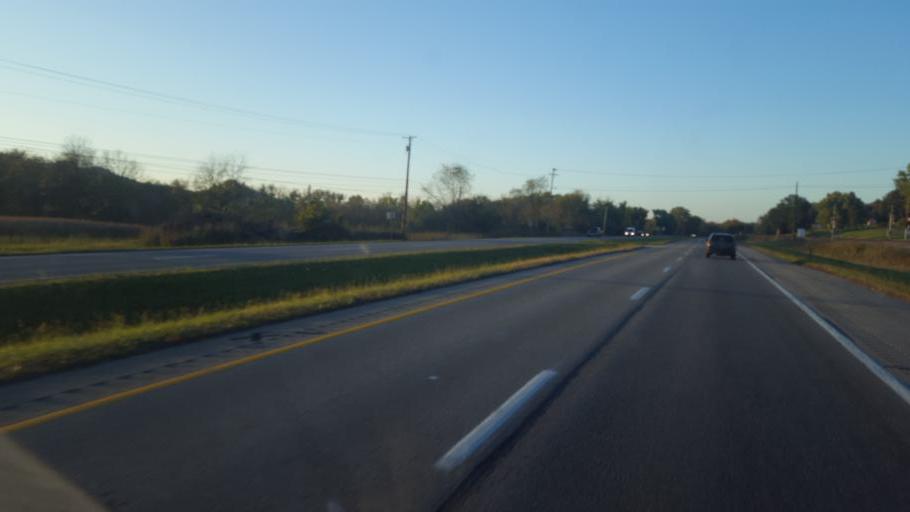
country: US
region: Ohio
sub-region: Scioto County
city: Lucasville
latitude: 38.9255
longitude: -83.0206
